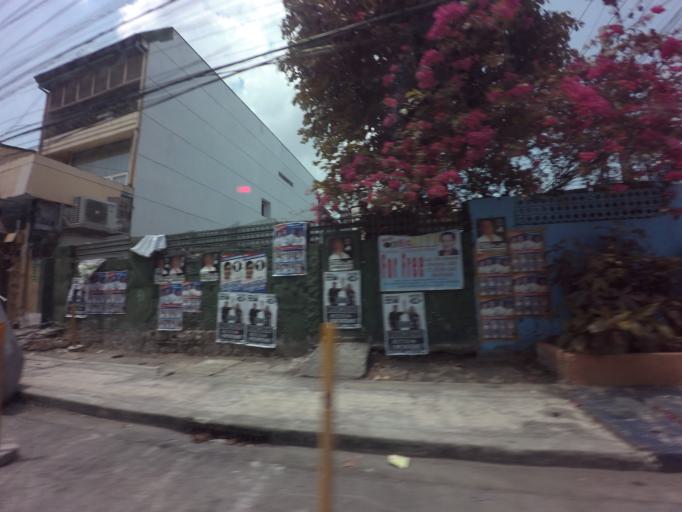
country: PH
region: Metro Manila
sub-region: Mandaluyong
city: Mandaluyong City
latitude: 14.5736
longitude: 121.0219
